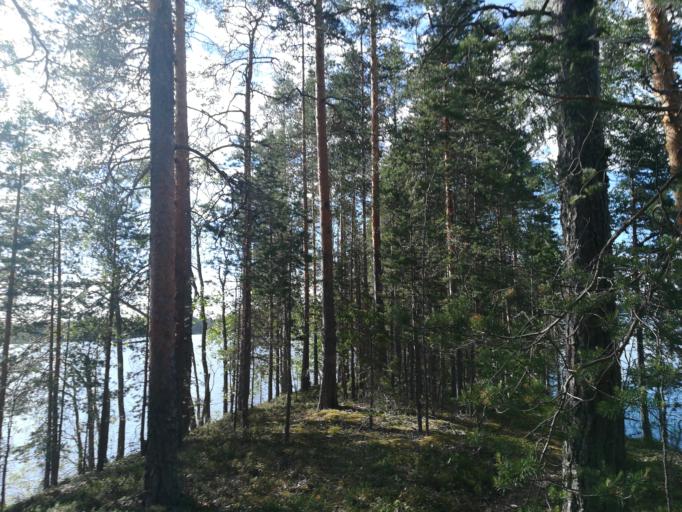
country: FI
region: Southern Savonia
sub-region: Savonlinna
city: Savonlinna
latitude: 61.6434
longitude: 28.7100
